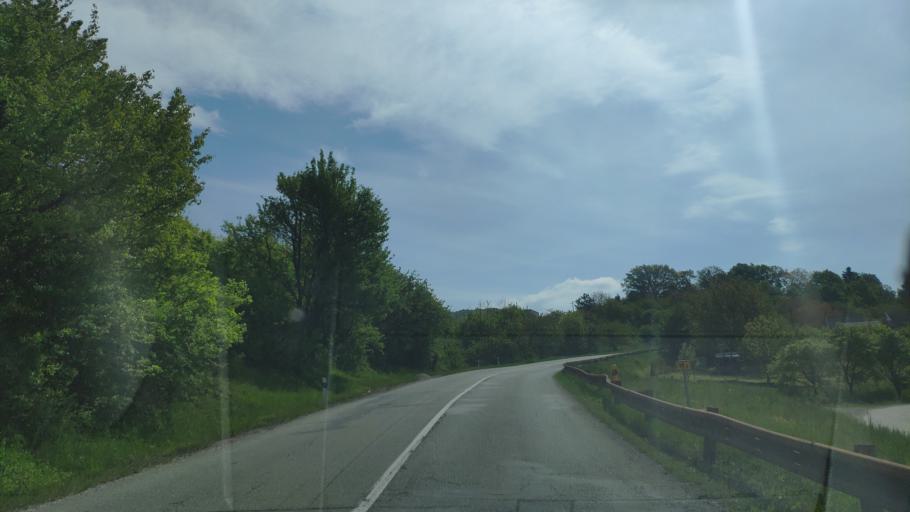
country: SK
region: Kosicky
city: Kosice
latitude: 48.6459
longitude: 21.4256
